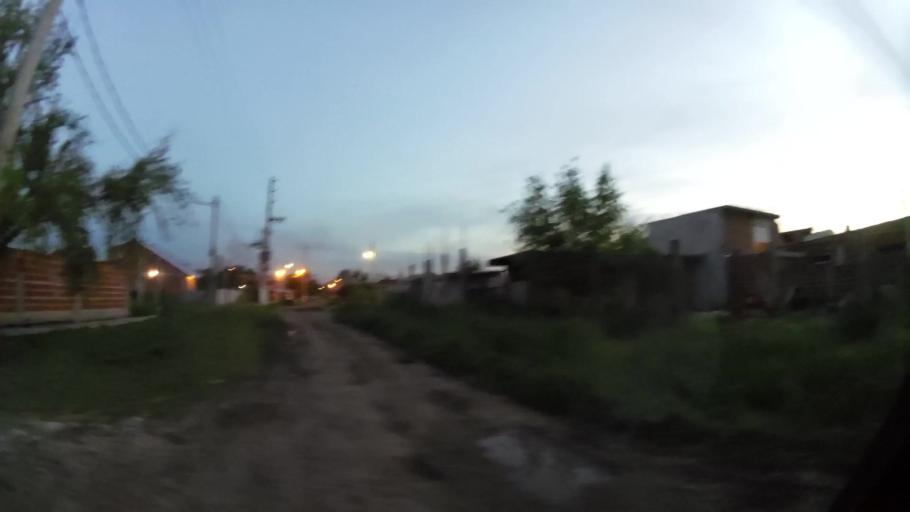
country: AR
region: Buenos Aires
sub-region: Partido de Quilmes
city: Quilmes
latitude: -34.8048
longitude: -58.2936
